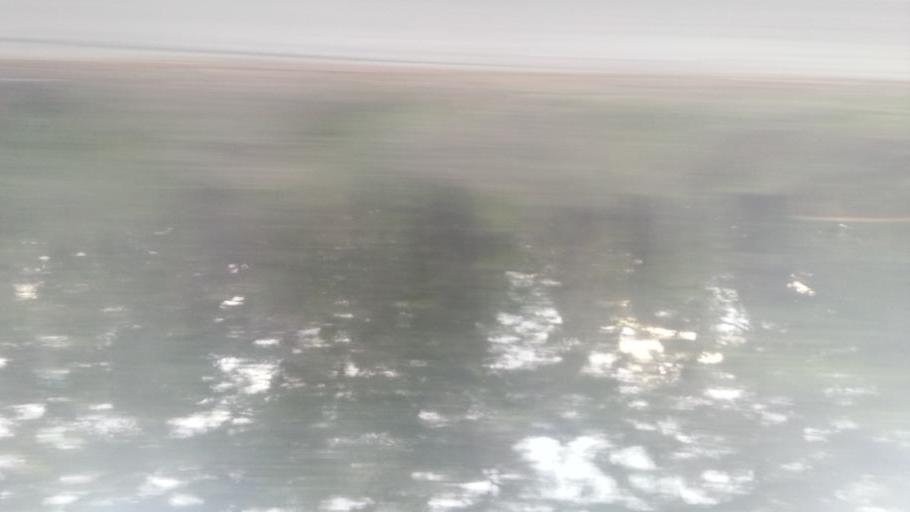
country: AU
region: New South Wales
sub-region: Wollongong
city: Mount Ousley
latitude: -34.3895
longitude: 150.8502
